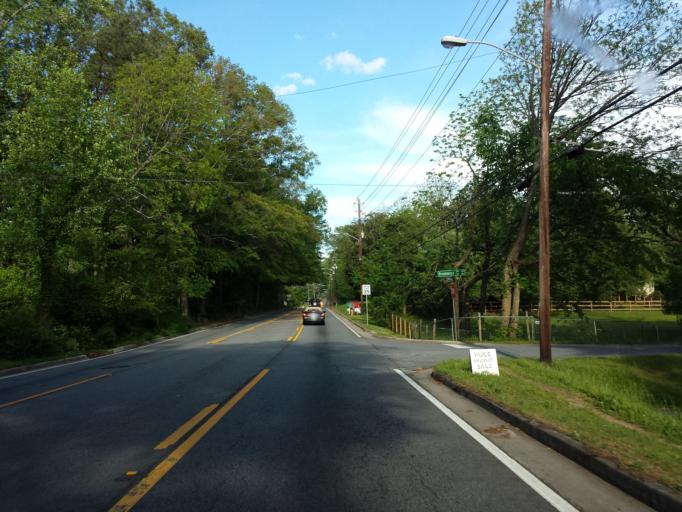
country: US
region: Georgia
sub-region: Cobb County
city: Marietta
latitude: 33.9518
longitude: -84.5677
